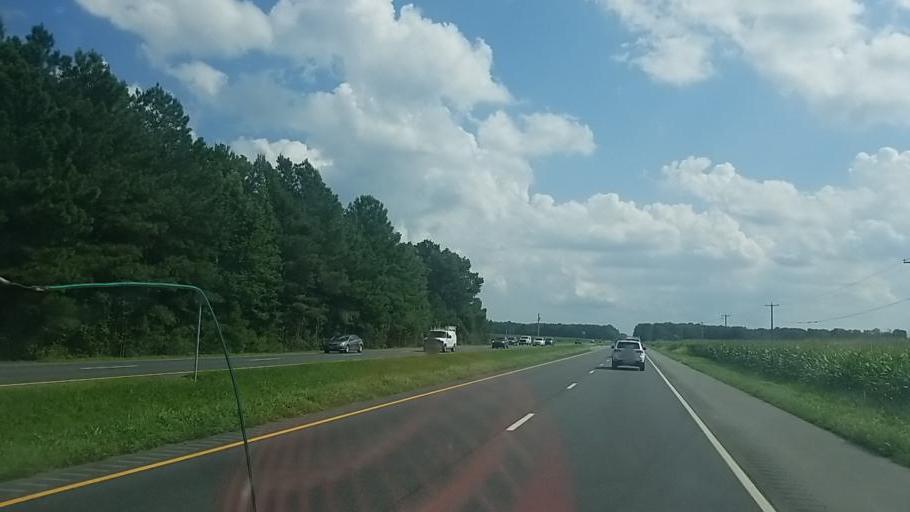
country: US
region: Delaware
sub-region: Sussex County
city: Selbyville
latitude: 38.4968
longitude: -75.2370
